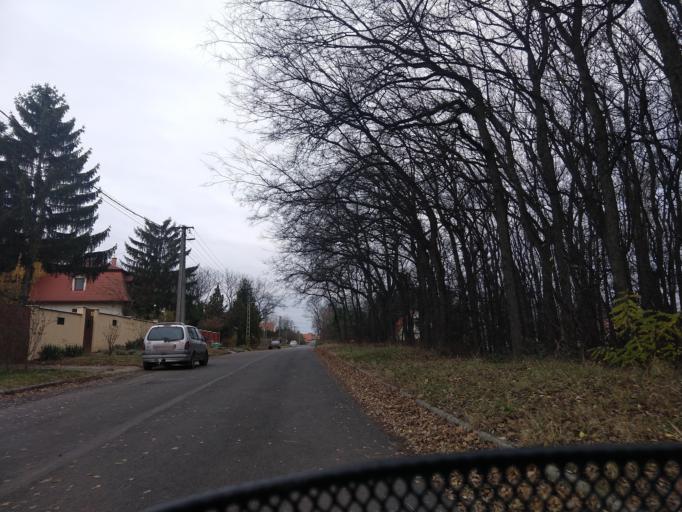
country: HU
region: Pest
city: Orbottyan
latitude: 47.6729
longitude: 19.2865
